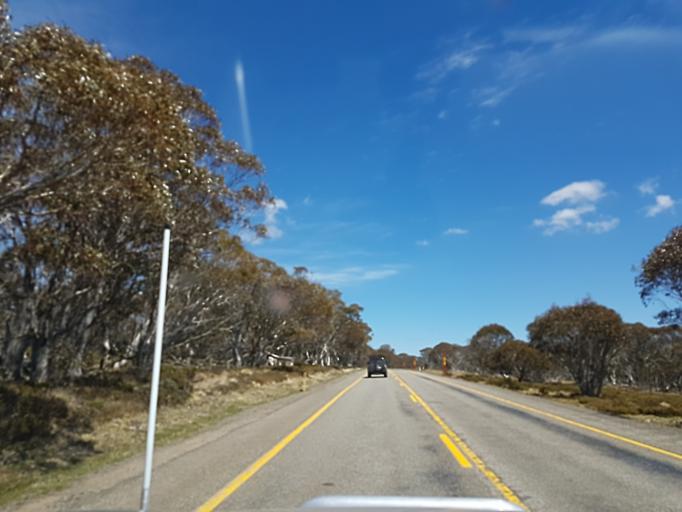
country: AU
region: Victoria
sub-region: Alpine
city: Mount Beauty
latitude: -37.0220
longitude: 147.2551
